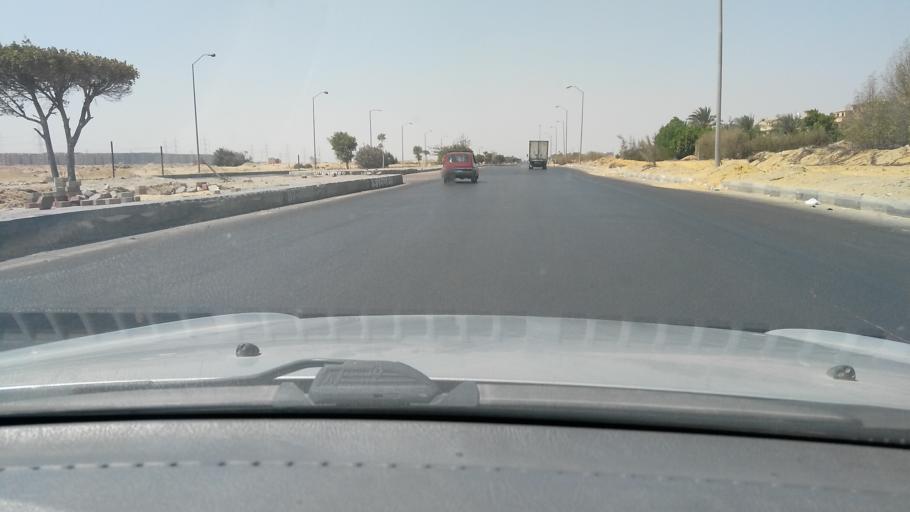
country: EG
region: Al Jizah
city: Madinat Sittah Uktubar
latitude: 29.9659
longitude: 30.9751
